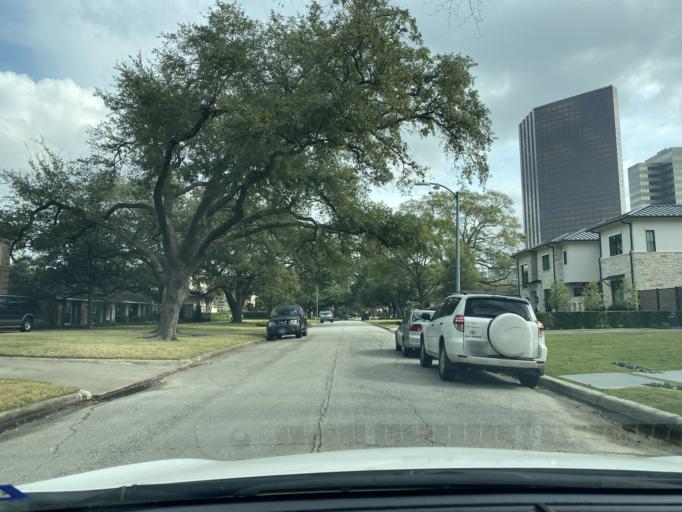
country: US
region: Texas
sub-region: Harris County
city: Hunters Creek Village
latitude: 29.7513
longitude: -95.4765
